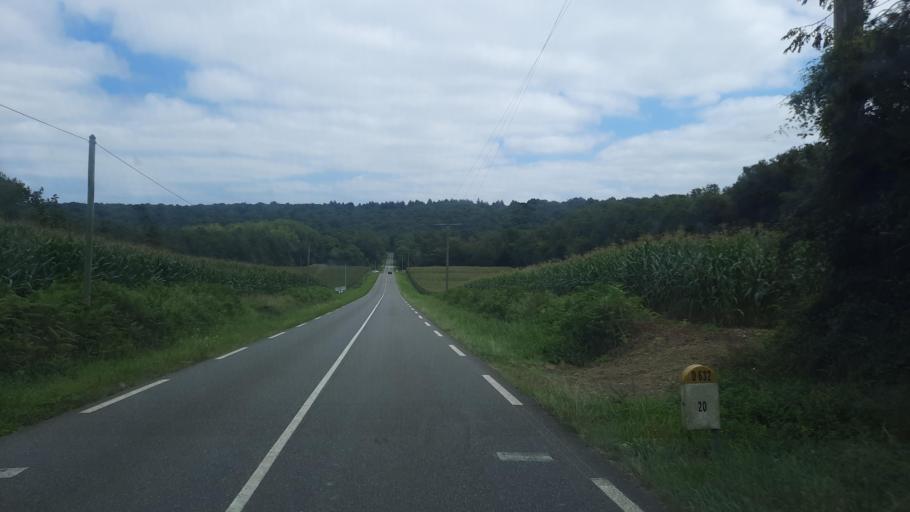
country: FR
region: Midi-Pyrenees
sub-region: Departement des Hautes-Pyrenees
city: Trie-sur-Baise
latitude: 43.2993
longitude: 0.4222
